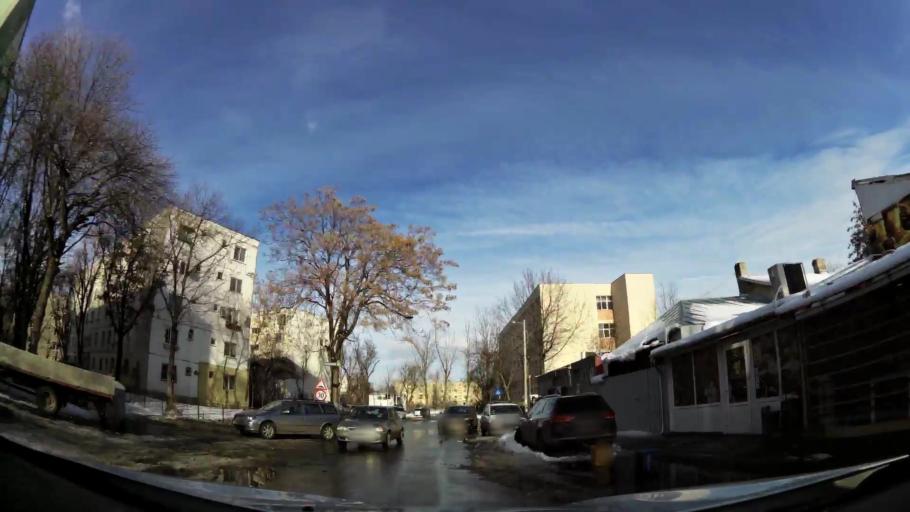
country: RO
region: Bucuresti
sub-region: Municipiul Bucuresti
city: Bucuresti
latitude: 44.3855
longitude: 26.0962
